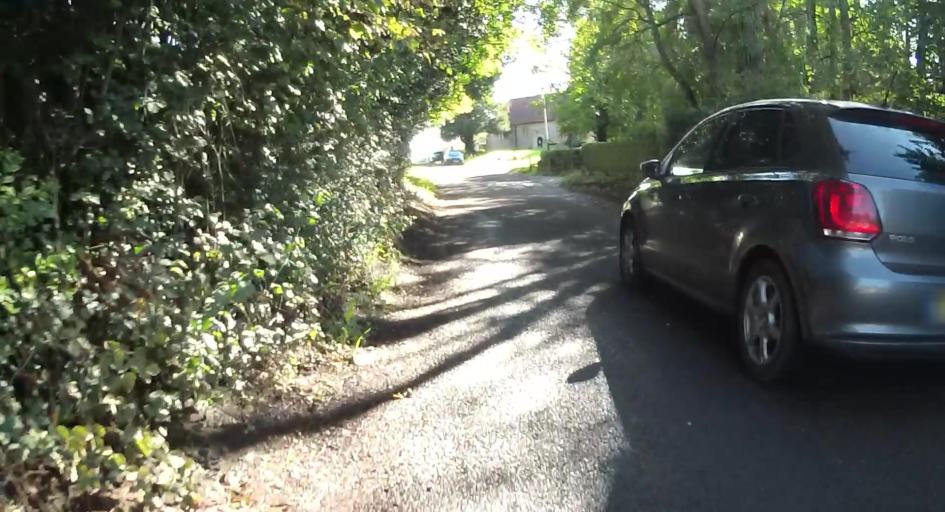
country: GB
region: England
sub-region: Hampshire
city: Old Basing
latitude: 51.2632
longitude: -0.9979
